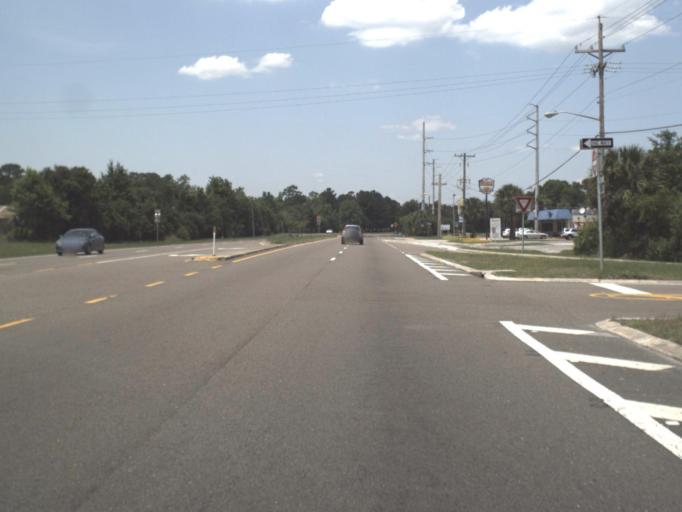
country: US
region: Florida
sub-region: Duval County
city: Jacksonville
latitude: 30.4085
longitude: -81.6502
